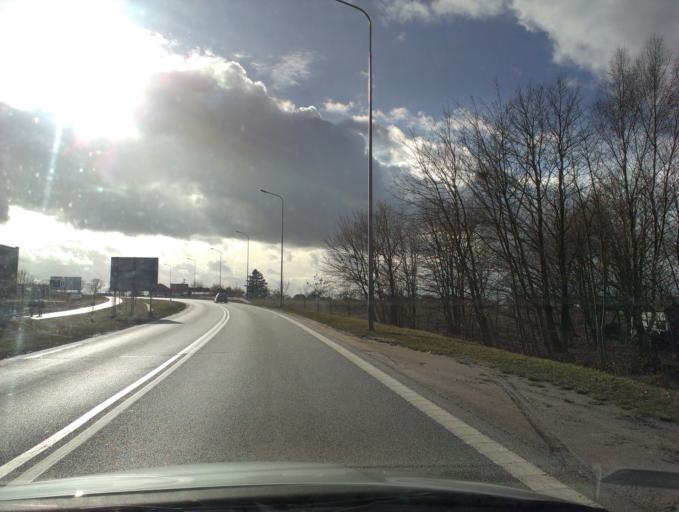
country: PL
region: Pomeranian Voivodeship
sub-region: Powiat czluchowski
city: Czluchow
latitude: 53.6690
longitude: 17.3503
